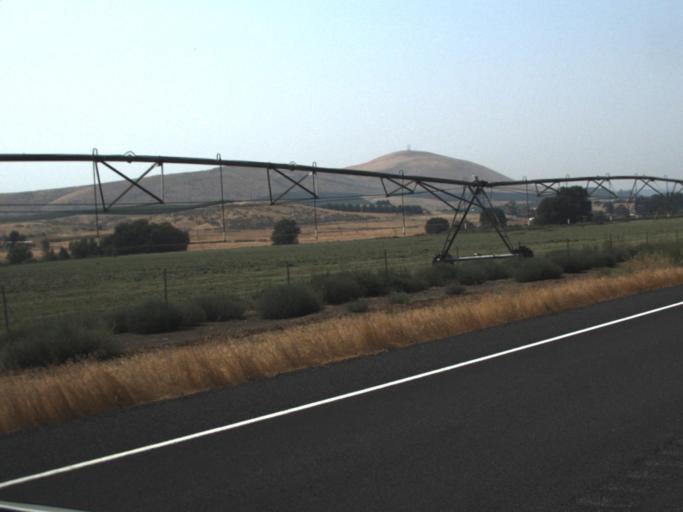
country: US
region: Washington
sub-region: Yakima County
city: Zillah
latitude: 46.5318
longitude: -120.2794
